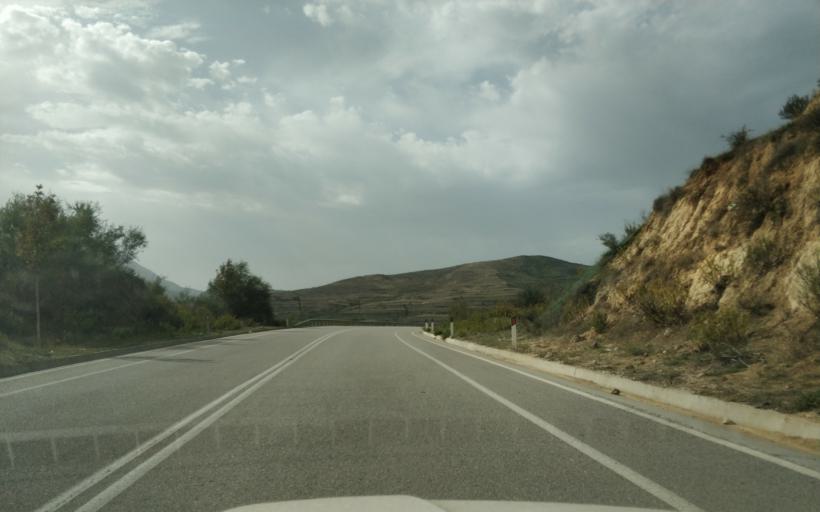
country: AL
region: Gjirokaster
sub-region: Rrethi i Tepelenes
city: Krahes
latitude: 40.3983
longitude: 19.8671
